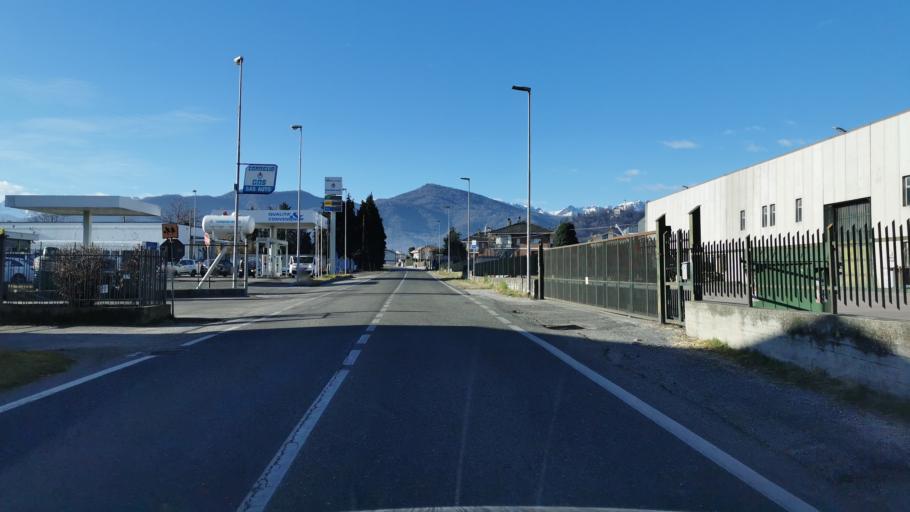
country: IT
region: Piedmont
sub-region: Provincia di Cuneo
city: Caraglio
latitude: 44.4253
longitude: 7.4422
